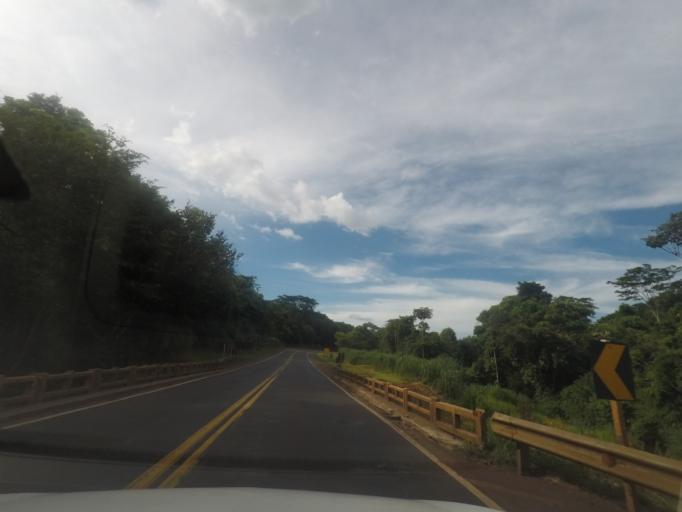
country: BR
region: Minas Gerais
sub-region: Monte Alegre De Minas
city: Monte Alegre de Minas
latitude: -19.0503
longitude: -49.0113
